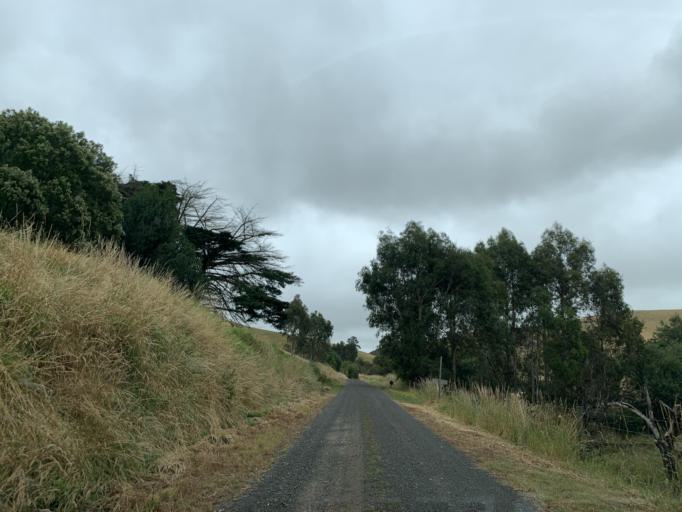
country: AU
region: Victoria
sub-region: Baw Baw
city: Warragul
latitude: -38.3309
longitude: 145.8501
